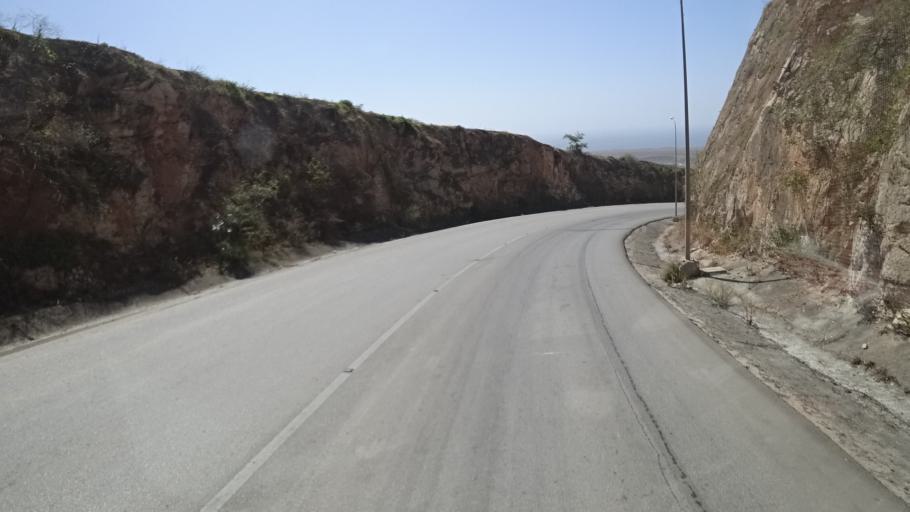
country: OM
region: Zufar
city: Salalah
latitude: 17.0666
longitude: 54.4484
